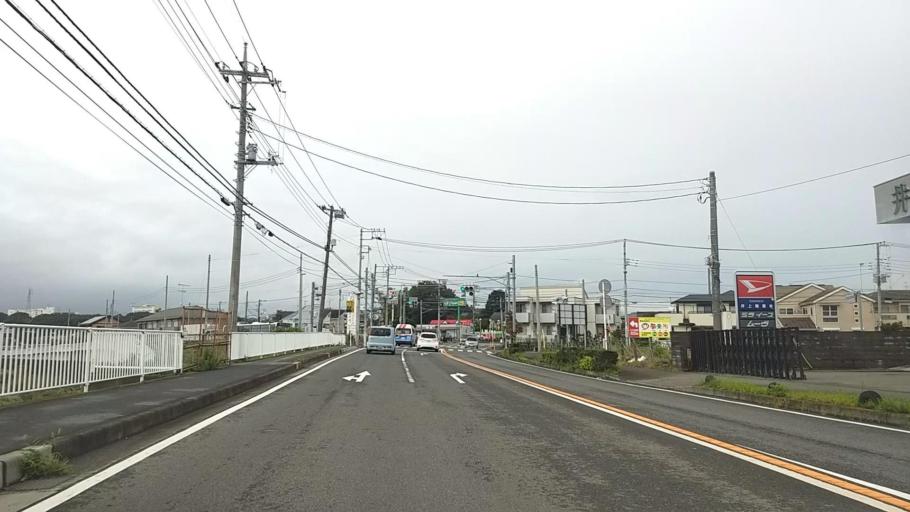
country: JP
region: Kanagawa
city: Atsugi
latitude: 35.4356
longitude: 139.3521
